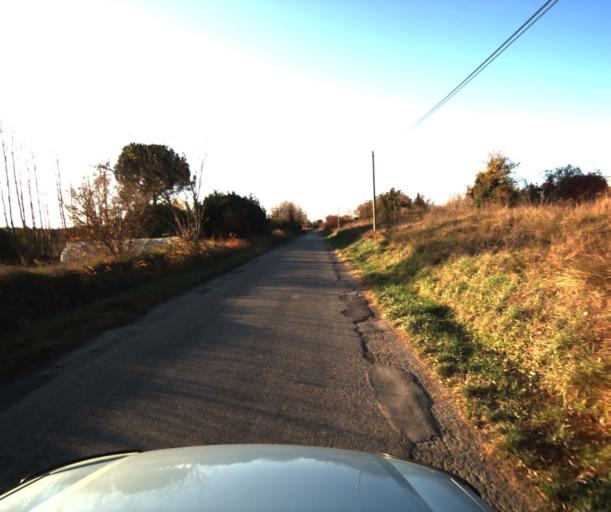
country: FR
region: Provence-Alpes-Cote d'Azur
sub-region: Departement du Vaucluse
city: Pertuis
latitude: 43.6793
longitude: 5.5175
